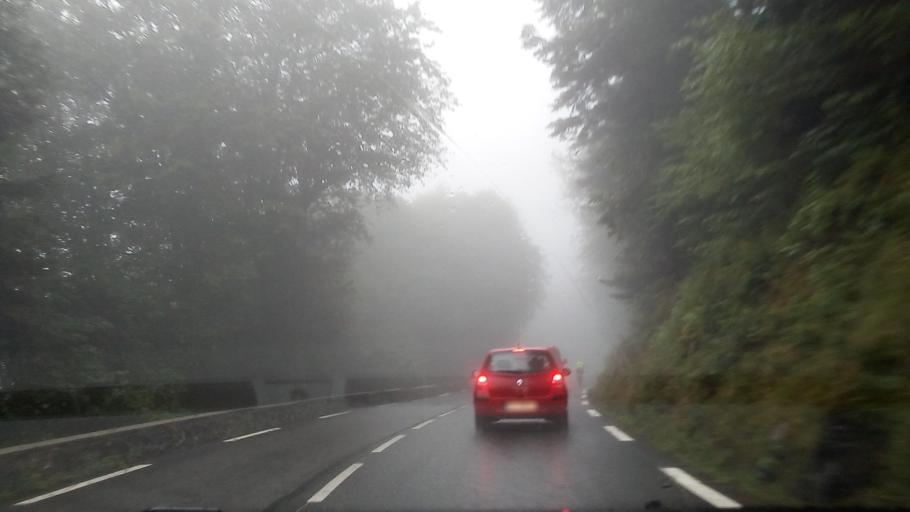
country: FR
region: Midi-Pyrenees
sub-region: Departement des Hautes-Pyrenees
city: Campan
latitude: 42.9213
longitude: 0.2045
